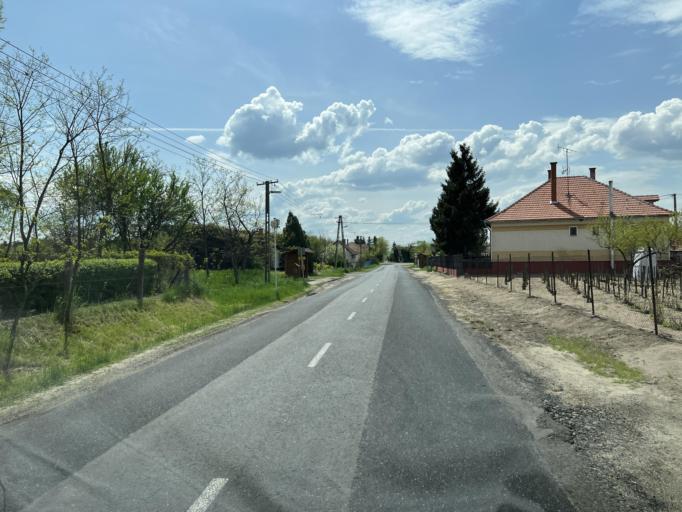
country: HU
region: Pest
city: Csemo
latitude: 47.1355
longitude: 19.7359
